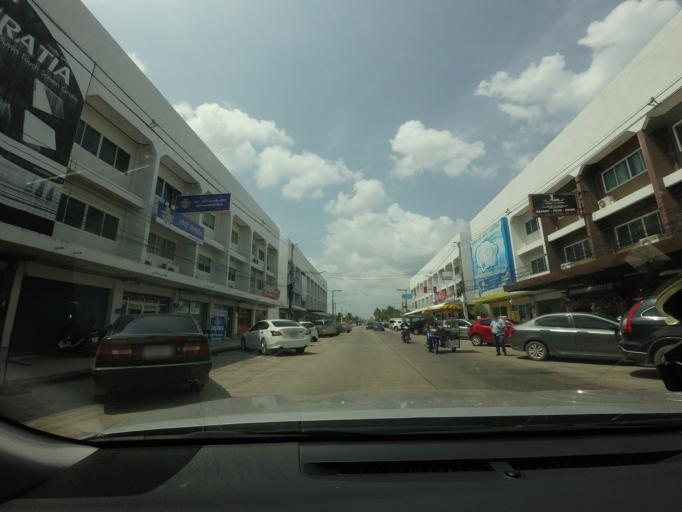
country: TH
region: Nakhon Si Thammarat
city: Nakhon Si Thammarat
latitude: 8.4287
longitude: 99.9800
